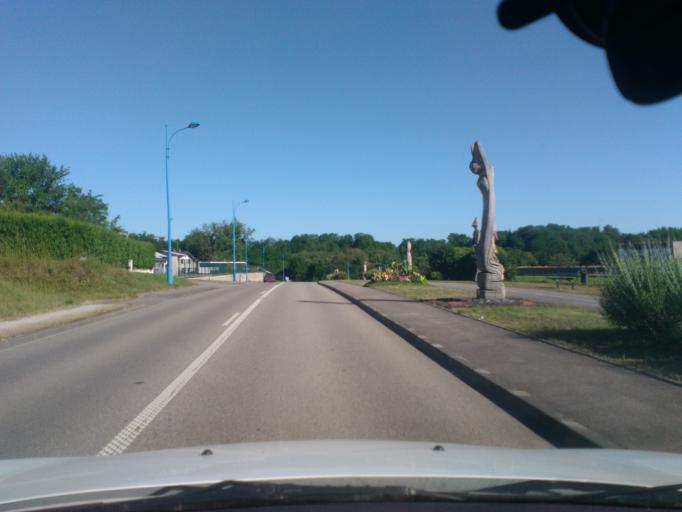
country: FR
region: Lorraine
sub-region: Departement des Vosges
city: Mirecourt
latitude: 48.2853
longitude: 6.1294
